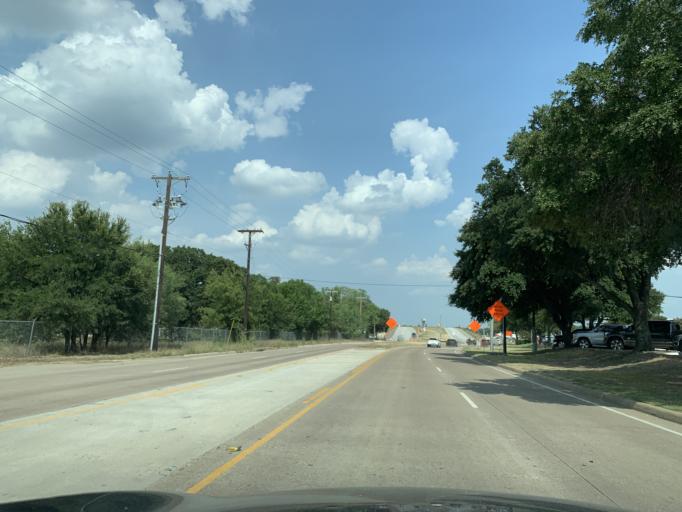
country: US
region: Texas
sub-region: Tarrant County
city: Richland Hills
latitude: 32.7979
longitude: -97.2160
